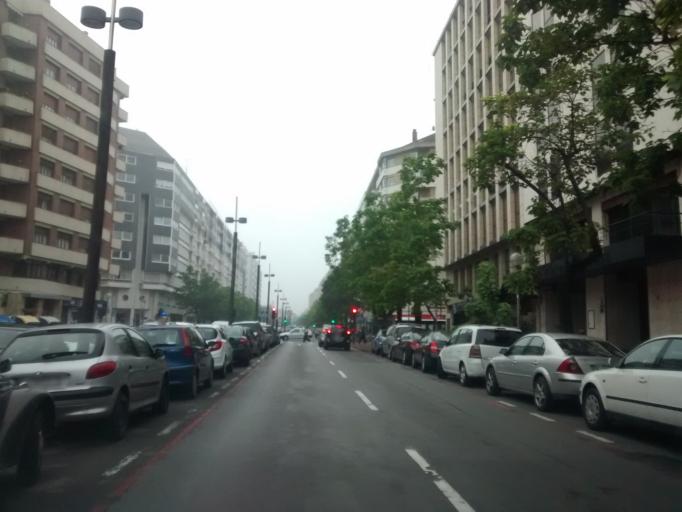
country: ES
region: Basque Country
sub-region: Provincia de Alava
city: Gasteiz / Vitoria
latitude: 42.8480
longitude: -2.6817
